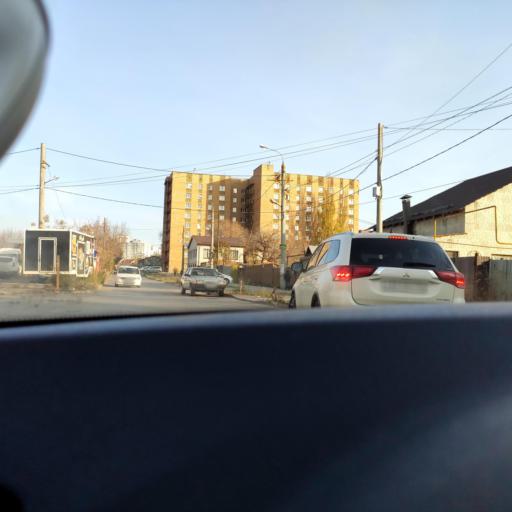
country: RU
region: Samara
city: Samara
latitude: 53.2228
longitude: 50.1754
